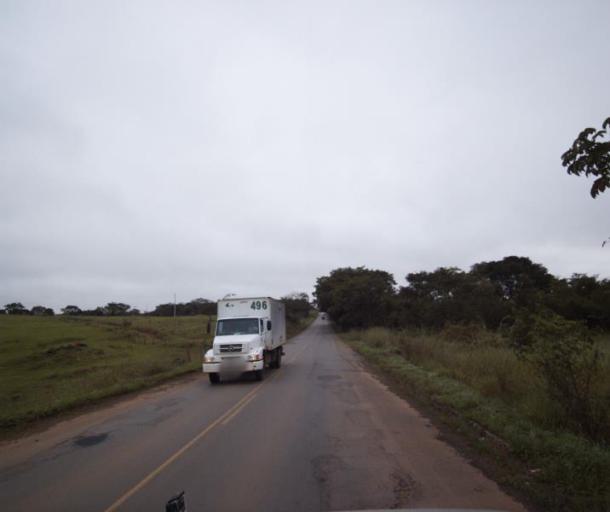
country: BR
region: Goias
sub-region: Pirenopolis
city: Pirenopolis
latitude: -15.9034
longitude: -48.8001
